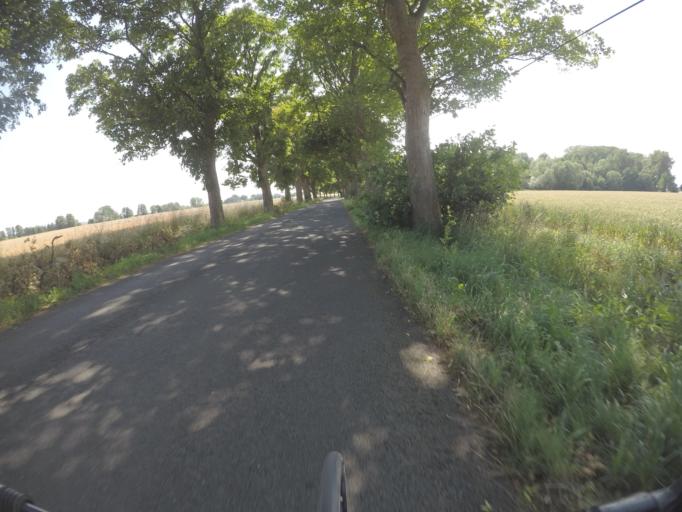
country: DE
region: Mecklenburg-Vorpommern
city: Gingst
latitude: 54.4429
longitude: 13.1875
